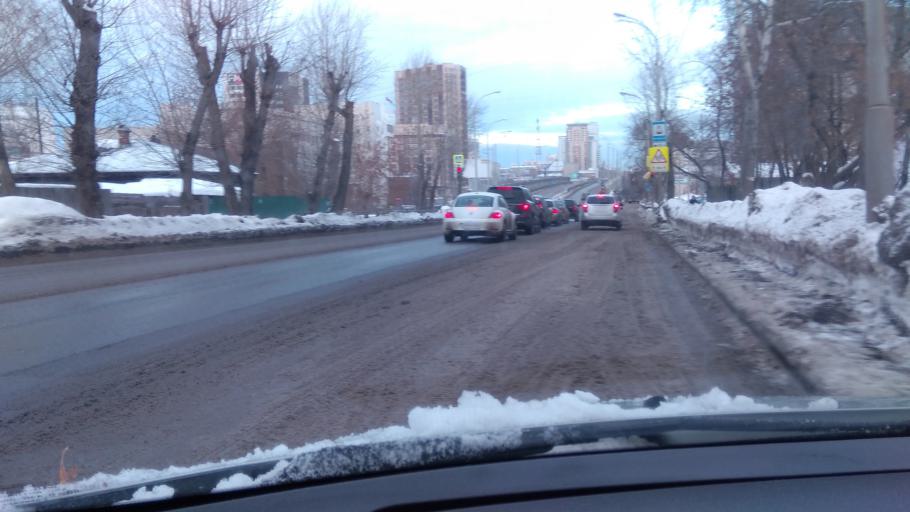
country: RU
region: Sverdlovsk
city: Yekaterinburg
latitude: 56.8110
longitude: 60.5910
